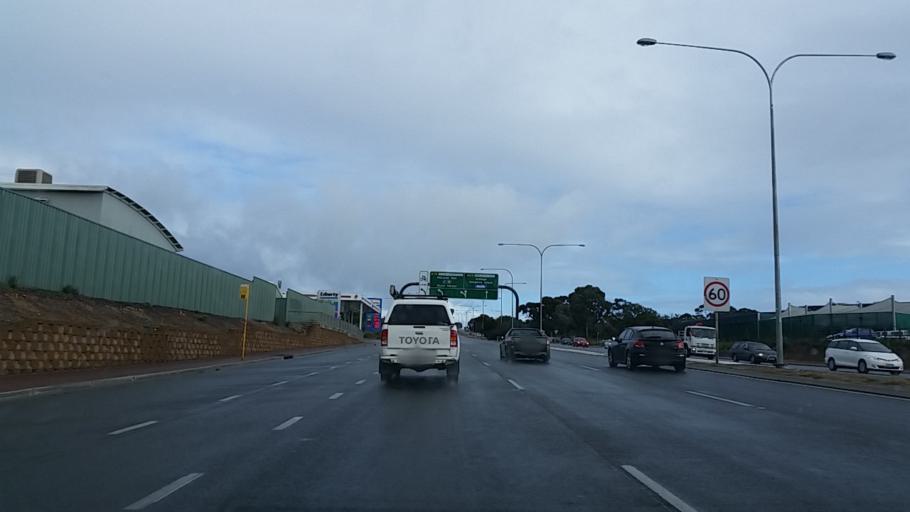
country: AU
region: South Australia
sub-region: Onkaparinga
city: Noarlunga
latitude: -35.1803
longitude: 138.4960
